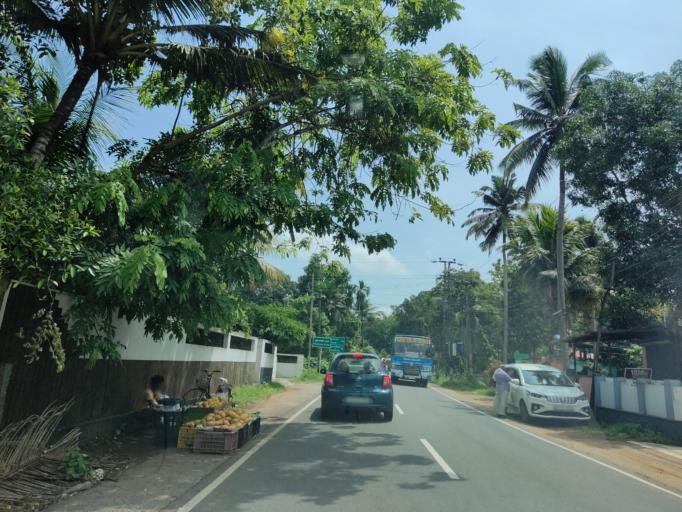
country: IN
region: Kerala
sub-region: Alappuzha
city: Chengannur
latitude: 9.3077
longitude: 76.5899
